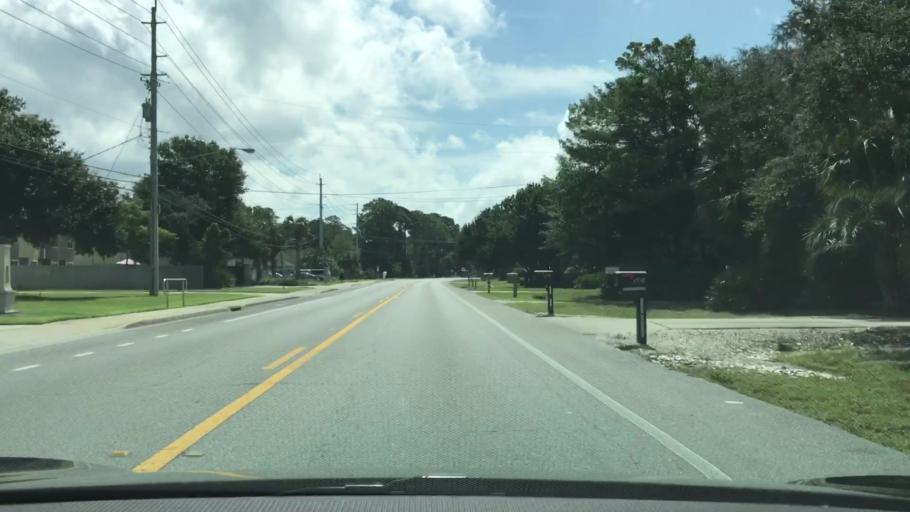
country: US
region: Florida
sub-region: Bay County
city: Lower Grand Lagoon
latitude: 30.1570
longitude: -85.7578
